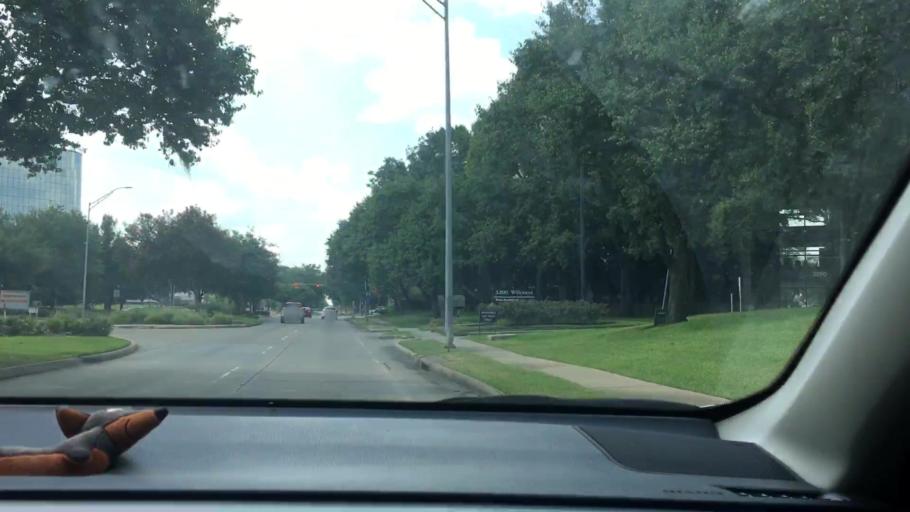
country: US
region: Texas
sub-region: Harris County
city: Bunker Hill Village
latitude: 29.7292
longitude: -95.5718
